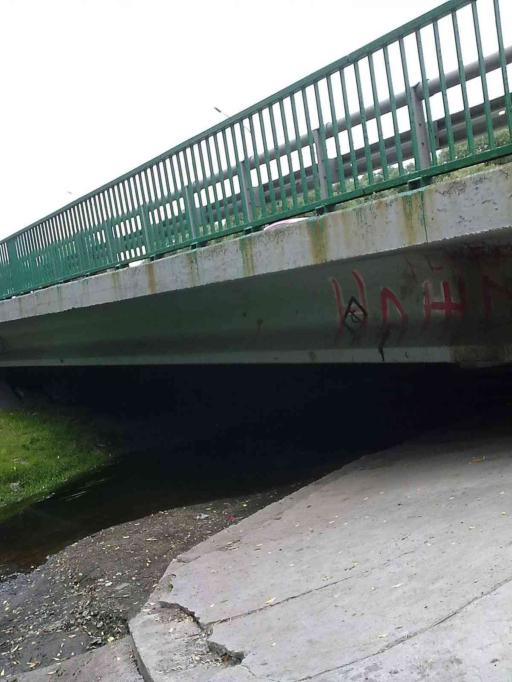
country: RU
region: Moskovskaya
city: Kommunarka
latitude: 55.5562
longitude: 37.4335
